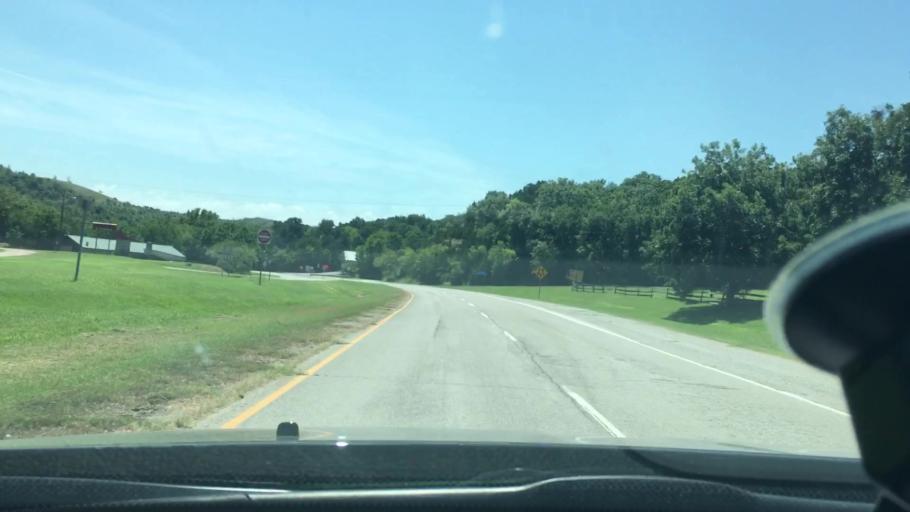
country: US
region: Oklahoma
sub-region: Murray County
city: Davis
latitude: 34.4479
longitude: -97.1356
